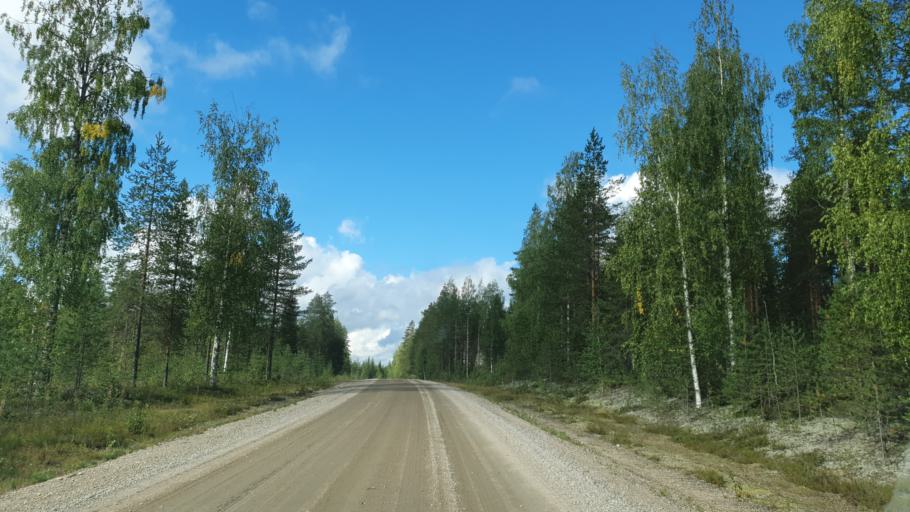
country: FI
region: Kainuu
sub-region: Kehys-Kainuu
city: Kuhmo
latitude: 63.9837
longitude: 29.2411
